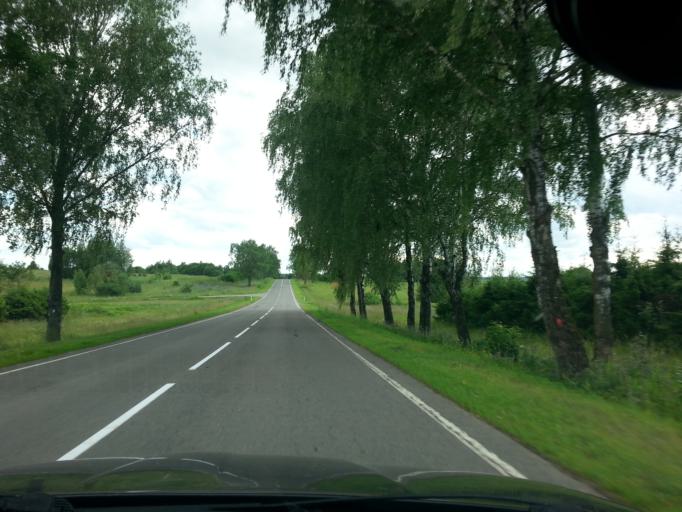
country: BY
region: Minsk
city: Svir
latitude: 54.9075
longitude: 26.3909
